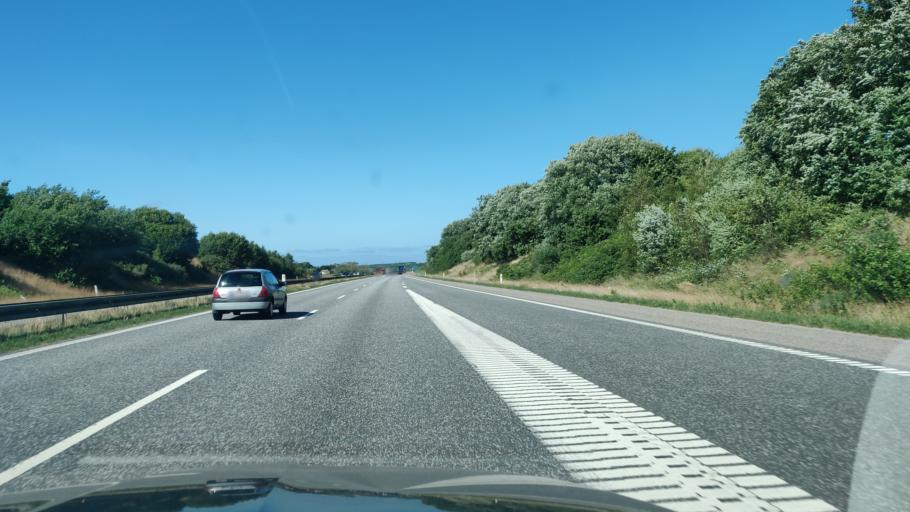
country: DK
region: North Denmark
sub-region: Mariagerfjord Kommune
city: Arden
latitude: 56.7873
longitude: 9.7008
